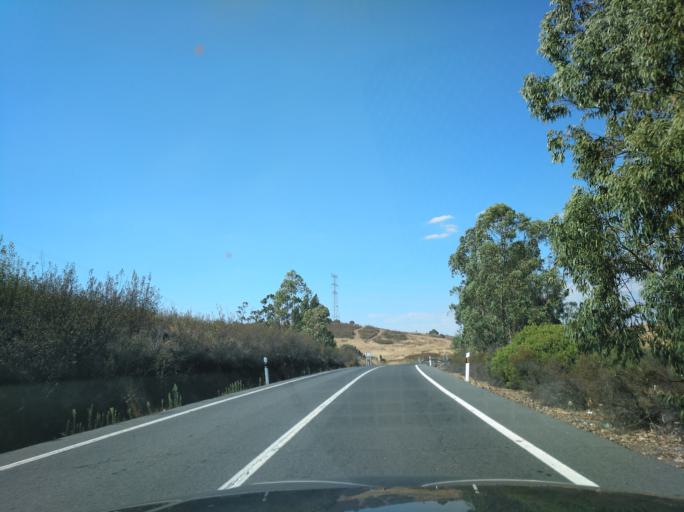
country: ES
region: Andalusia
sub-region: Provincia de Huelva
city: Alosno
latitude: 37.5090
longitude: -7.1329
